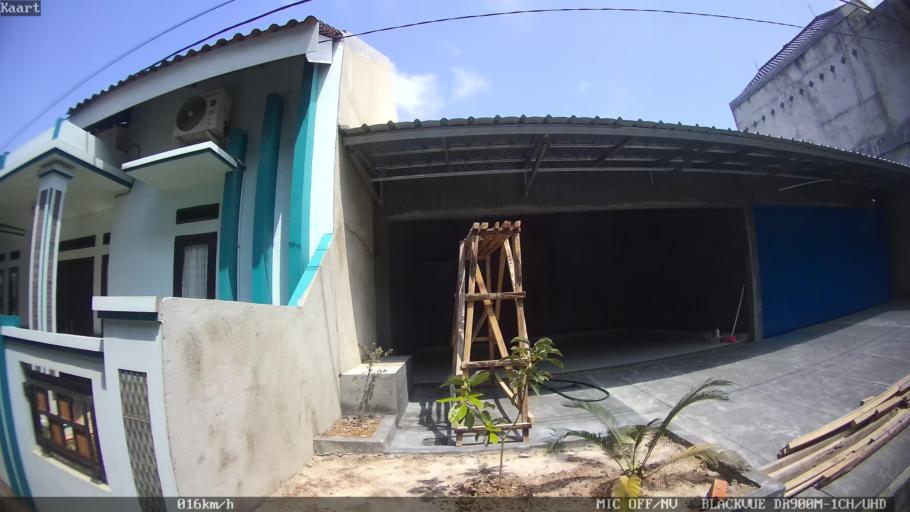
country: ID
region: Lampung
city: Kedaton
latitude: -5.3562
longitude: 105.2814
